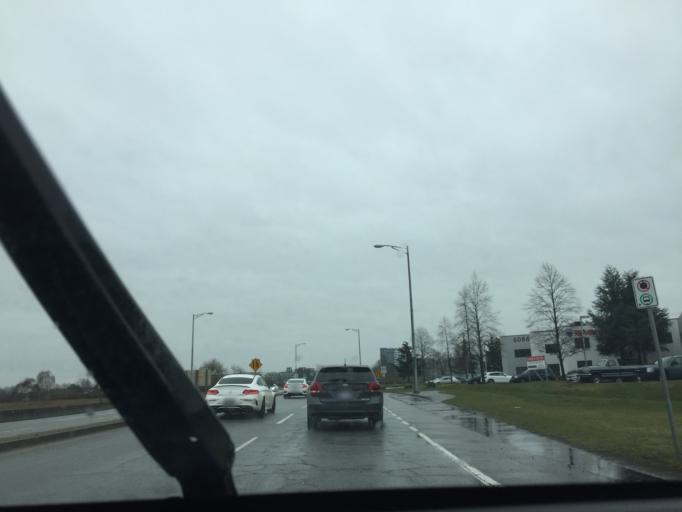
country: CA
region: British Columbia
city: Richmond
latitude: 49.1810
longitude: -123.1514
